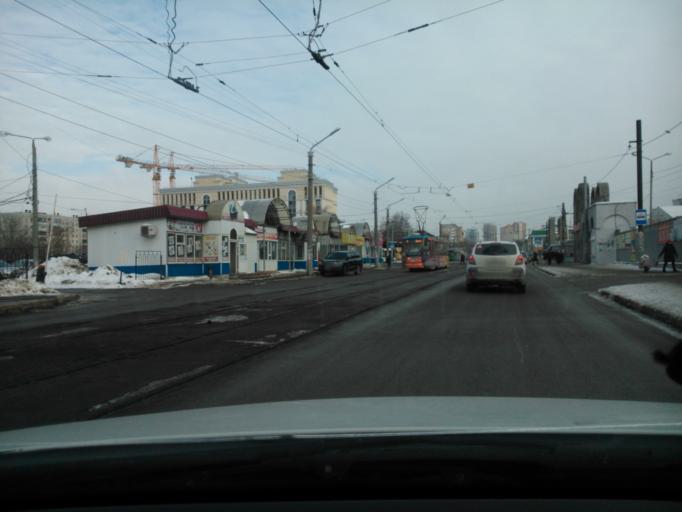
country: RU
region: Perm
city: Perm
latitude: 58.0023
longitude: 56.2221
